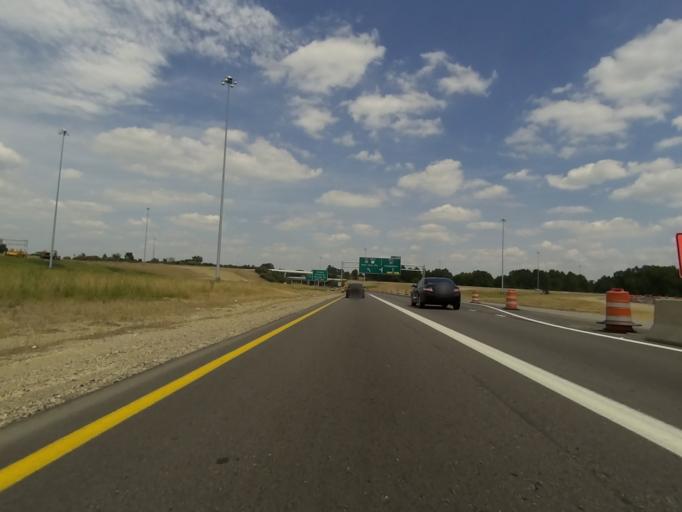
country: US
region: Ohio
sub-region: Trumbull County
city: Mineral Ridge
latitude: 41.1238
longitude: -80.7560
